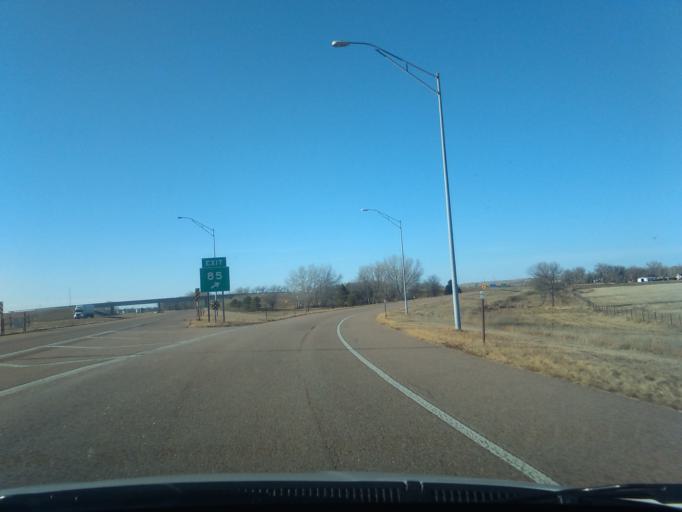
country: US
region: Nebraska
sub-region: Deuel County
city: Chappell
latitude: 41.0791
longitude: -102.4700
